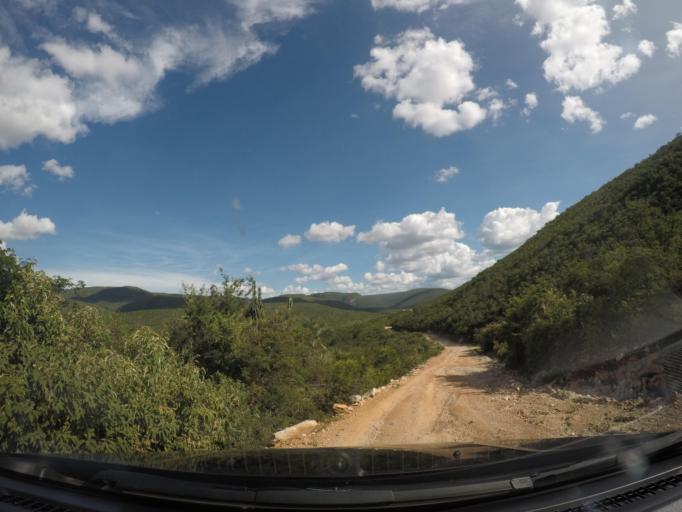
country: BR
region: Bahia
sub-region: Barra Da Estiva
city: Barra da Estiva
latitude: -13.2046
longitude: -41.5936
